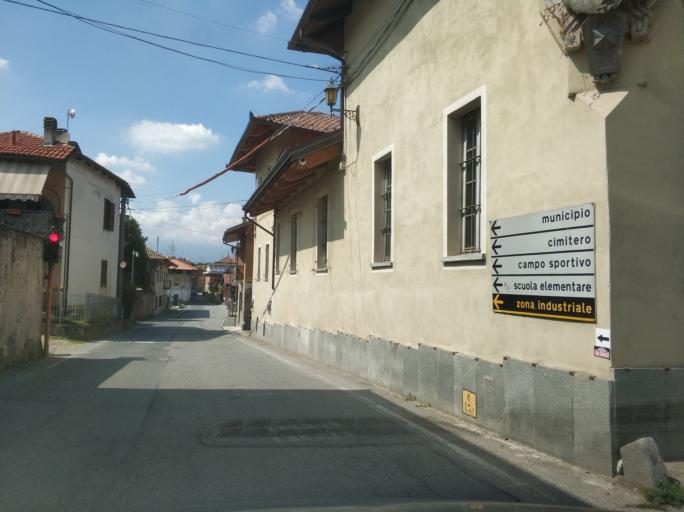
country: IT
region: Piedmont
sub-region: Provincia di Torino
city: Rivarossa
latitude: 45.2496
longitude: 7.7199
